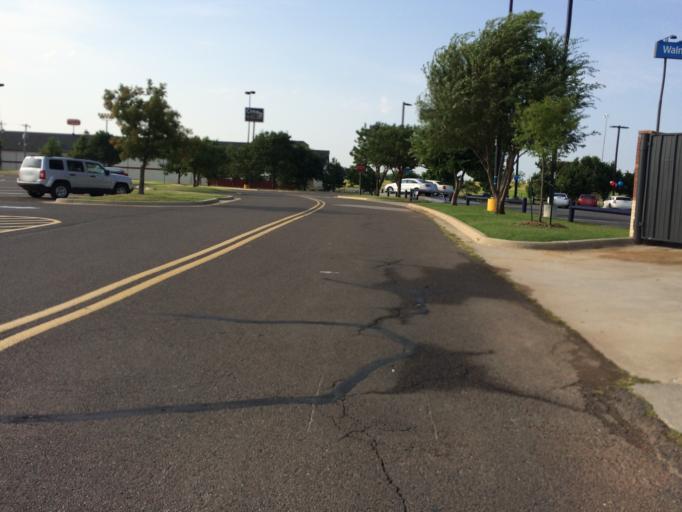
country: US
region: Oklahoma
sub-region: Cleveland County
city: Norman
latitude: 35.2213
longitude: -97.4839
